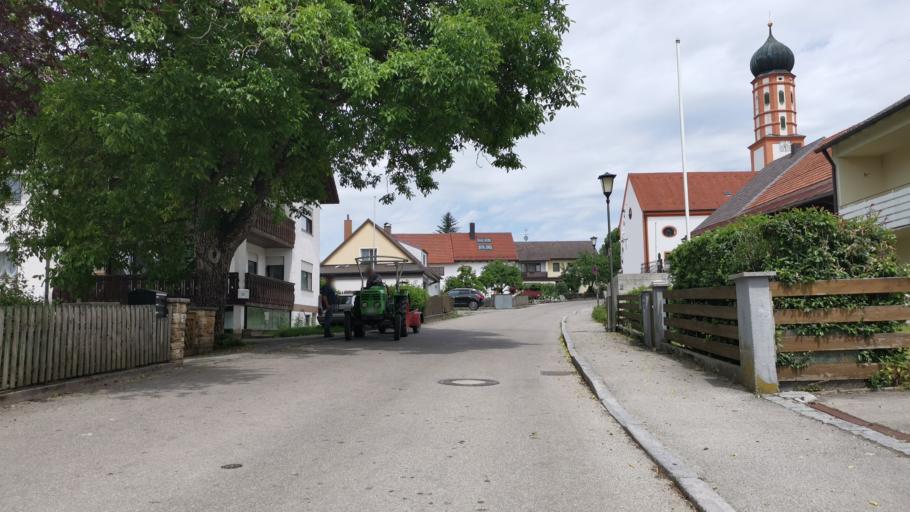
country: DE
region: Bavaria
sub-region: Upper Bavaria
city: Hattenhofen
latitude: 48.2209
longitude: 11.1179
